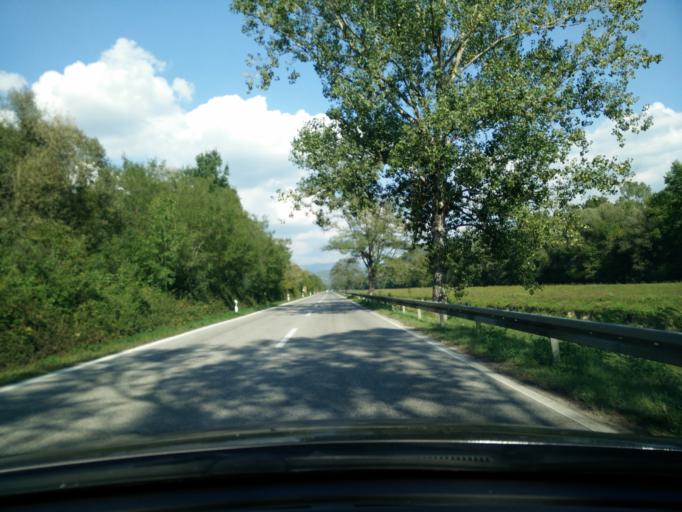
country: HR
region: Istarska
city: Karojba
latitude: 45.3489
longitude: 13.8449
